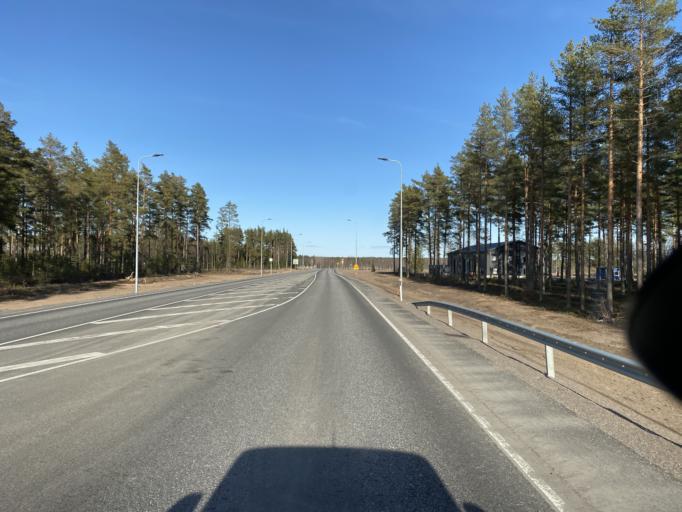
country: FI
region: Satakunta
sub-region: Rauma
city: Koeylioe
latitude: 61.1581
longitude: 22.2884
